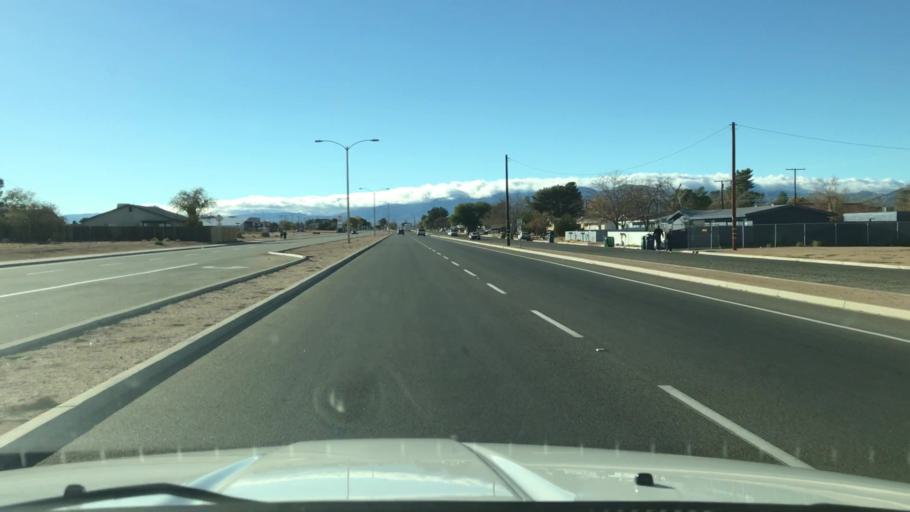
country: US
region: California
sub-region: Kern County
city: California City
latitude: 35.1258
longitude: -117.9885
